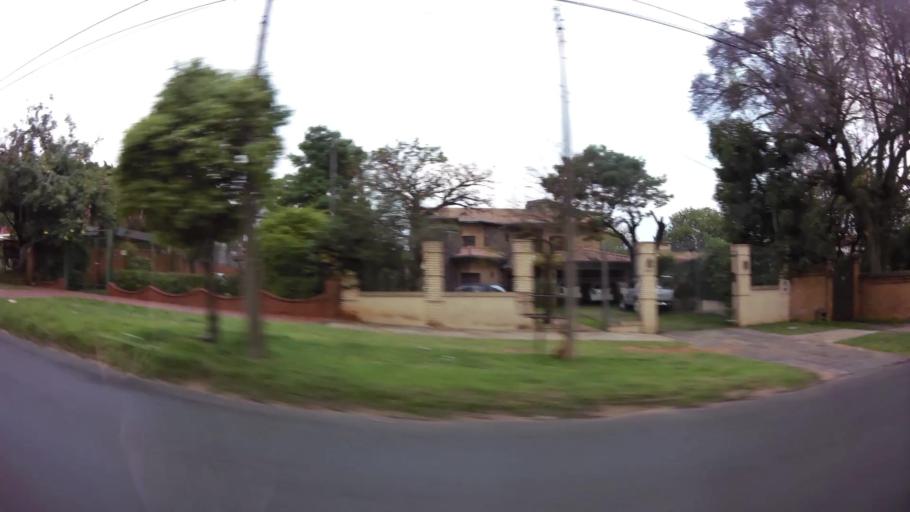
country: PY
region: Central
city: Lambare
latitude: -25.3327
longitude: -57.6302
